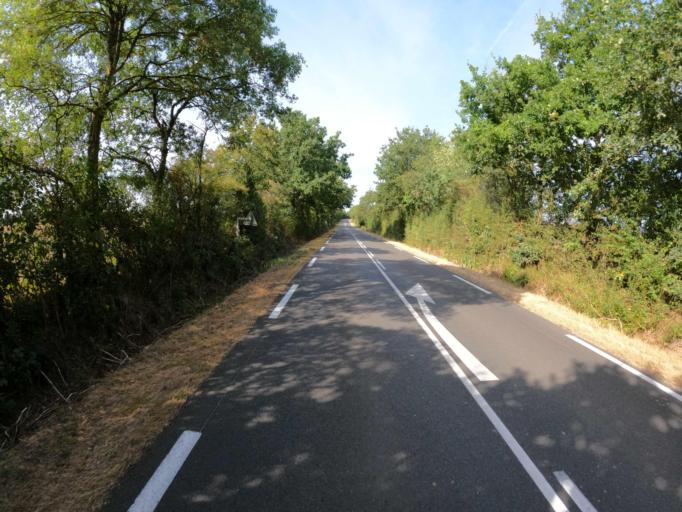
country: FR
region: Pays de la Loire
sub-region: Departement de la Vendee
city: Froidfond
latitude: 46.8505
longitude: -1.7286
